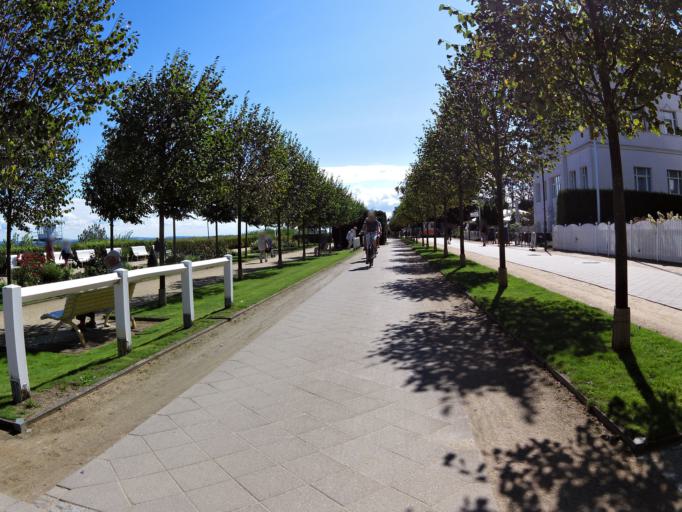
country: DE
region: Mecklenburg-Vorpommern
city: Seebad Bansin
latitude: 53.9742
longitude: 14.1432
